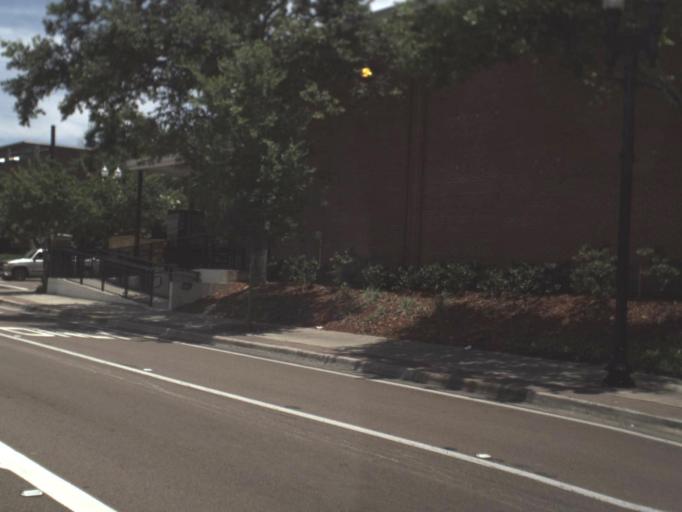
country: US
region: Florida
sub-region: Duval County
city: Jacksonville
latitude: 30.3312
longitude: -81.6516
